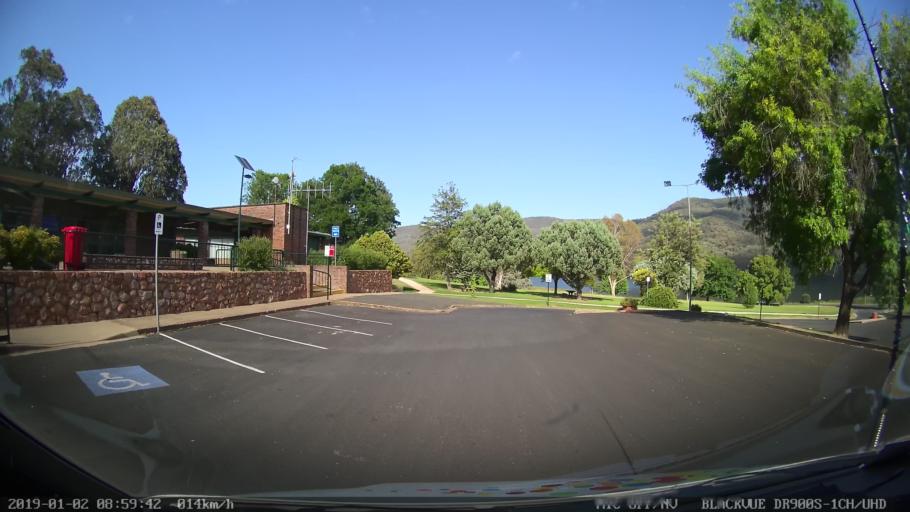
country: AU
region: New South Wales
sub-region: Tumut Shire
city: Tumut
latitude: -35.5824
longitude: 148.2975
